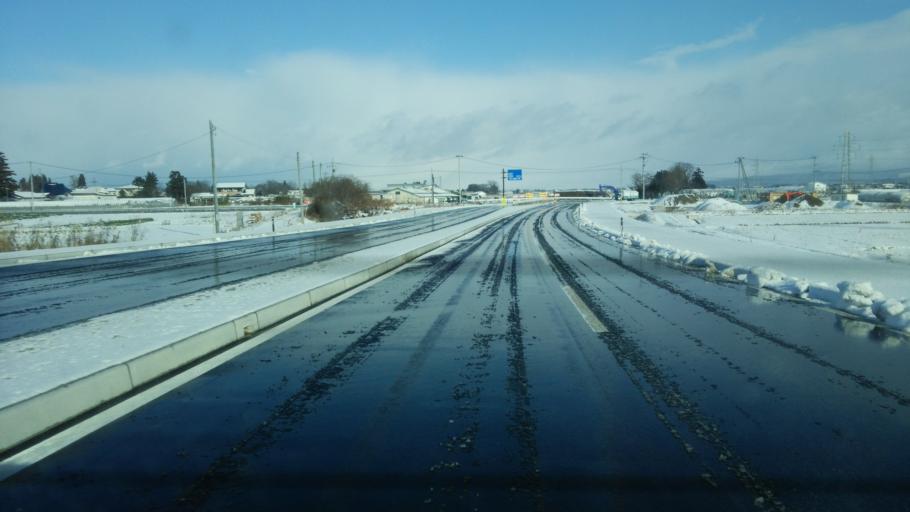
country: JP
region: Fukushima
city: Kitakata
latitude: 37.5023
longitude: 139.8963
